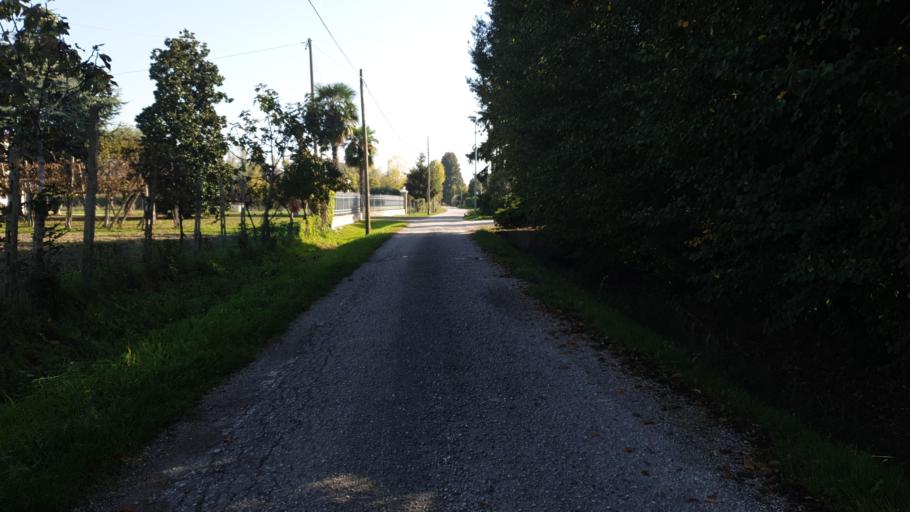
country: IT
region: Veneto
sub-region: Provincia di Venezia
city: Tombelle
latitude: 45.4060
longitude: 11.9832
